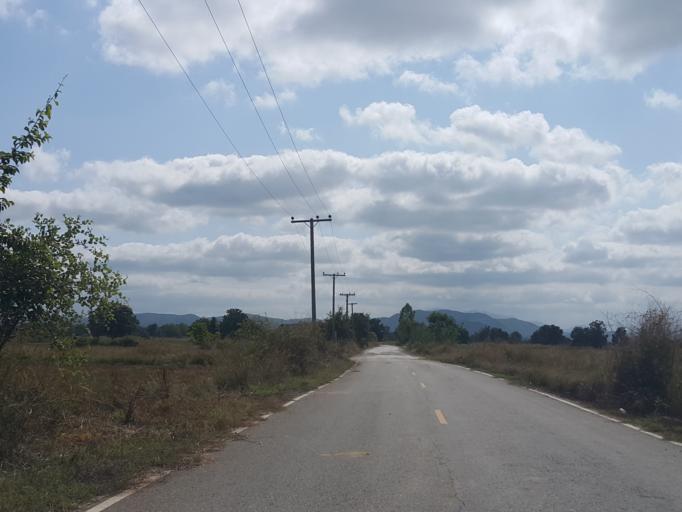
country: TH
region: Lamphun
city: Ban Thi
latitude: 18.5591
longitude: 99.0861
